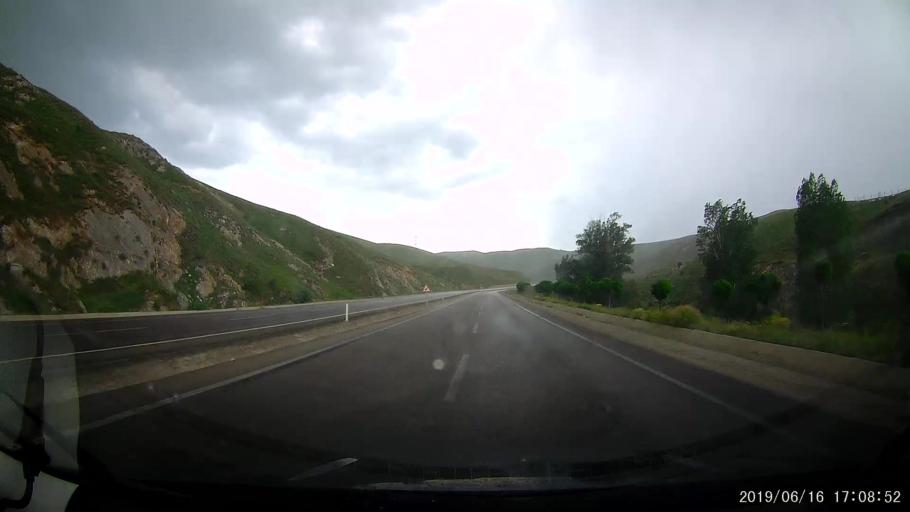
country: TR
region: Erzurum
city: Askale
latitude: 39.9023
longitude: 40.6569
